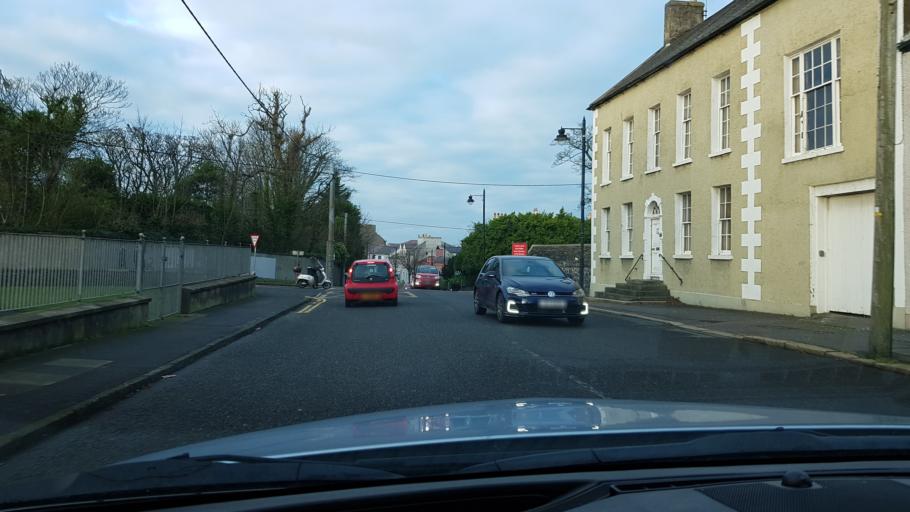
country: GB
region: Northern Ireland
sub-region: Down District
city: Donaghadee
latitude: 54.6403
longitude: -5.5344
